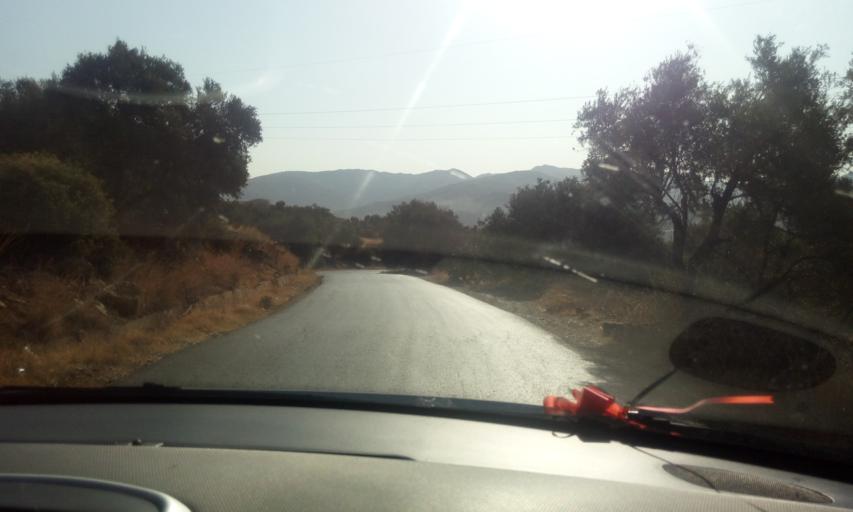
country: DZ
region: Tizi Ouzou
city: Chemini
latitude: 36.5644
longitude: 4.6195
